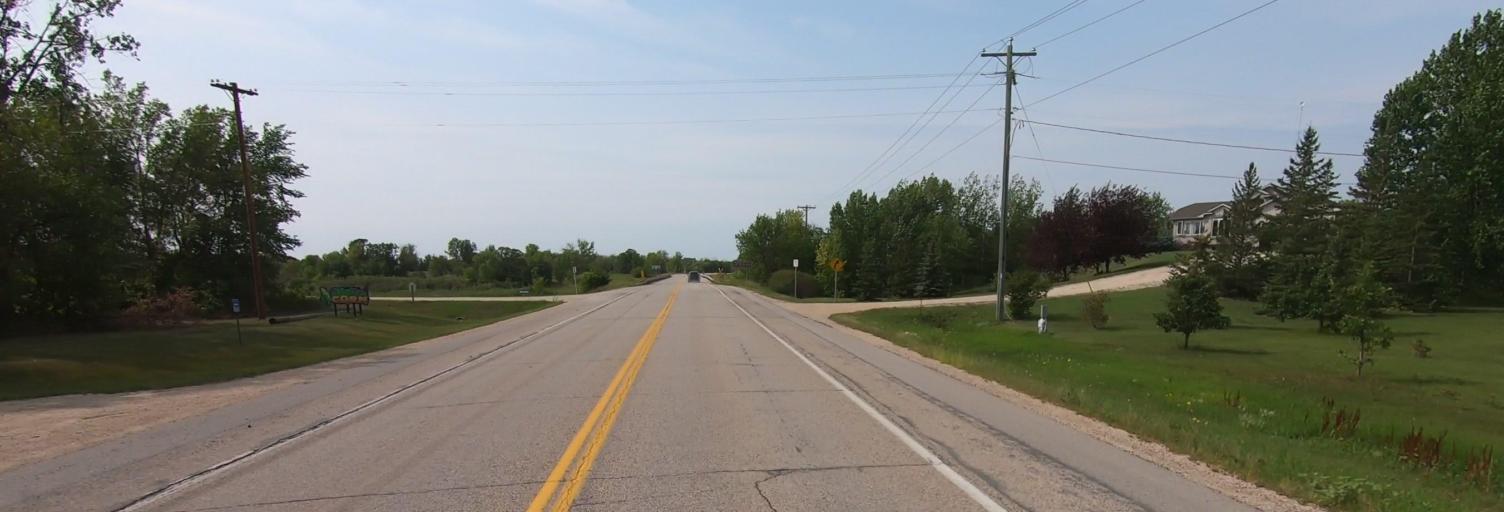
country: CA
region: Manitoba
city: Niverville
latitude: 49.6980
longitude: -97.0967
